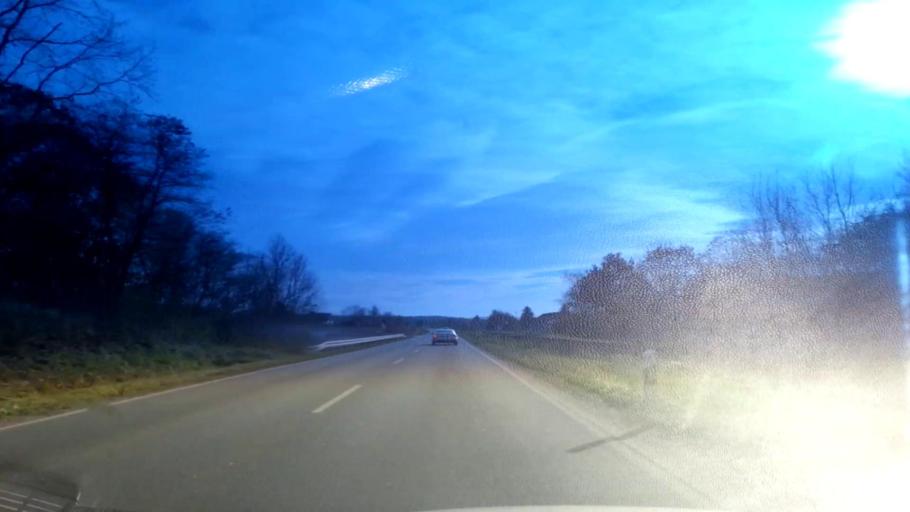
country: DE
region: Bavaria
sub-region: Upper Franconia
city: Reuth
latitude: 49.9703
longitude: 11.6873
